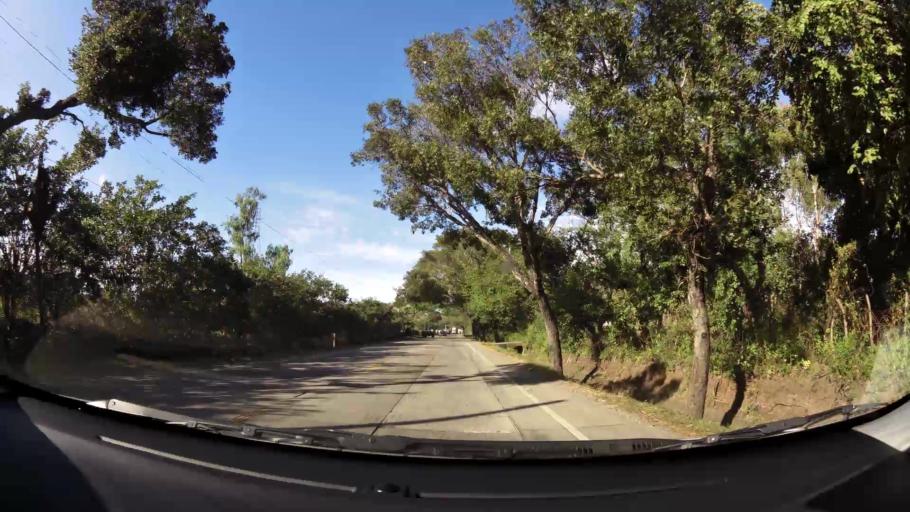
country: SV
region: Santa Ana
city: Texistepeque
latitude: 14.1044
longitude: -89.4998
